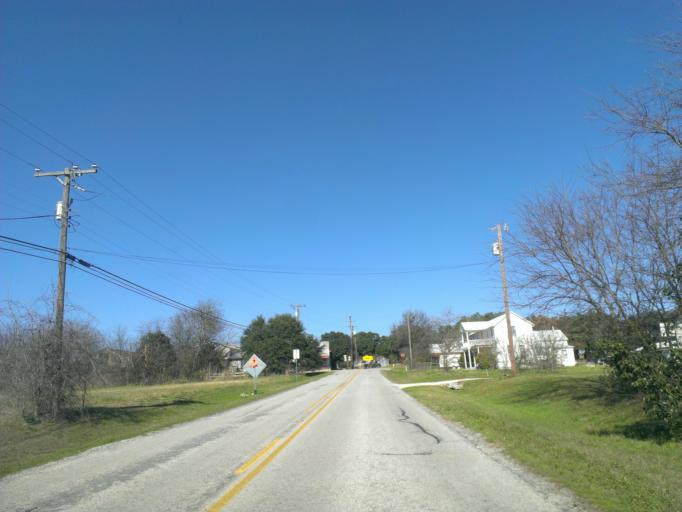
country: US
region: Texas
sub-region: Williamson County
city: Serenada
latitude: 30.7339
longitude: -97.5870
